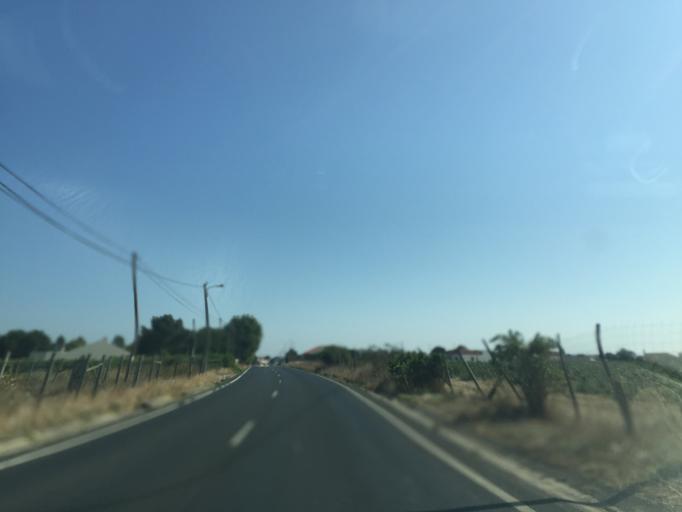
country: PT
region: Santarem
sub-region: Alpiarca
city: Alpiarca
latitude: 39.2713
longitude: -8.5672
